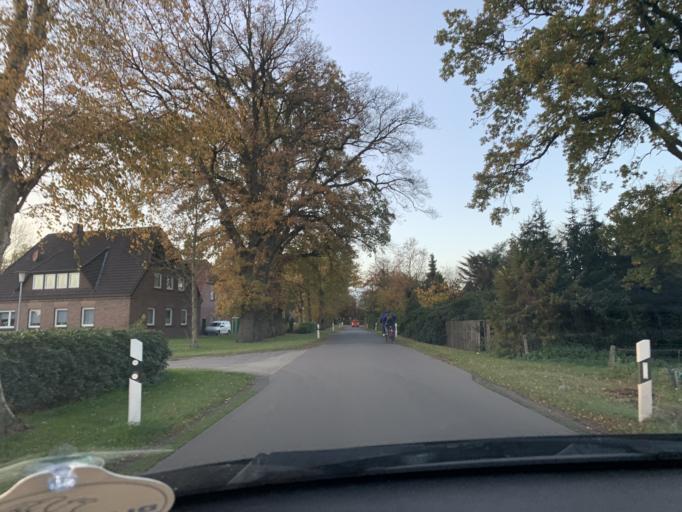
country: DE
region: Lower Saxony
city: Edewecht
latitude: 53.1238
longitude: 7.9963
